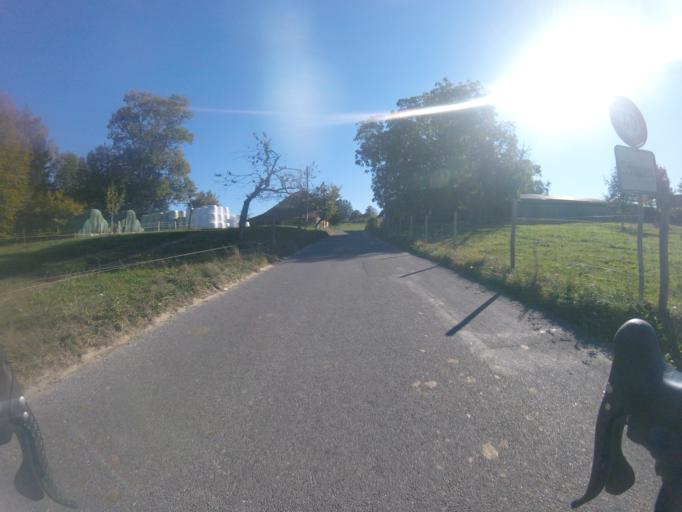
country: CH
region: Bern
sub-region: Seeland District
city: Schupfen
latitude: 47.0270
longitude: 7.3939
